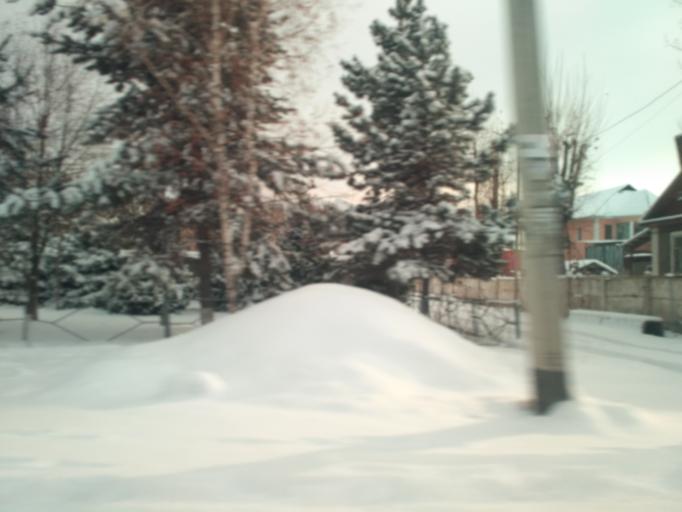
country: KZ
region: Almaty Qalasy
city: Almaty
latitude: 43.2162
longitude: 76.7681
